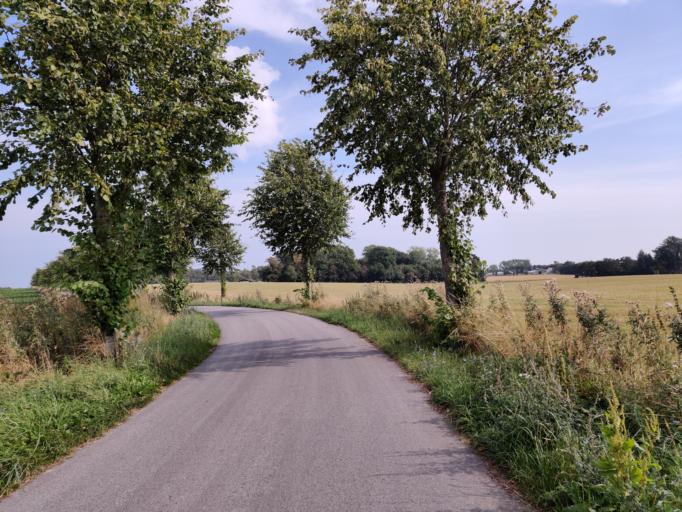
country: DK
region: Zealand
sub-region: Guldborgsund Kommune
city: Nykobing Falster
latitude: 54.7012
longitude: 11.9115
